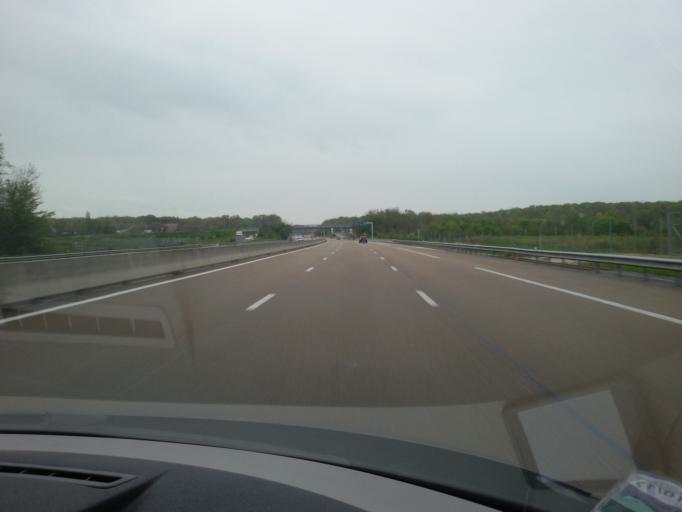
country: FR
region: Bourgogne
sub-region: Departement de la Cote-d'Or
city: Saint-Julien
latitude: 47.4185
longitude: 5.1749
